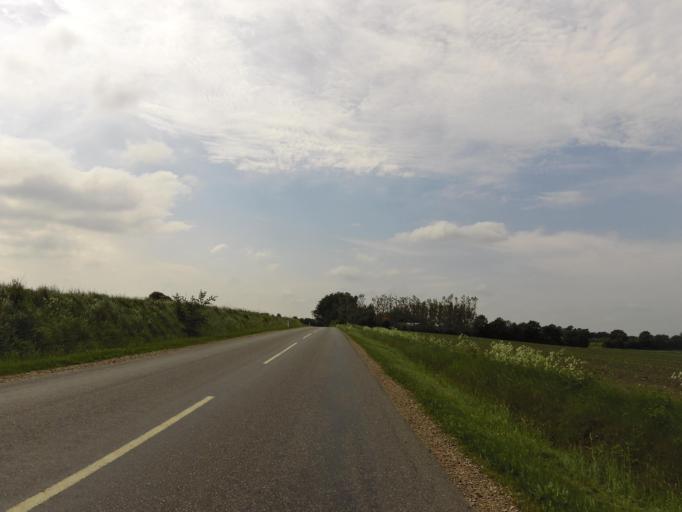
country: DK
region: South Denmark
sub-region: Haderslev Kommune
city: Gram
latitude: 55.2738
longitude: 9.1315
